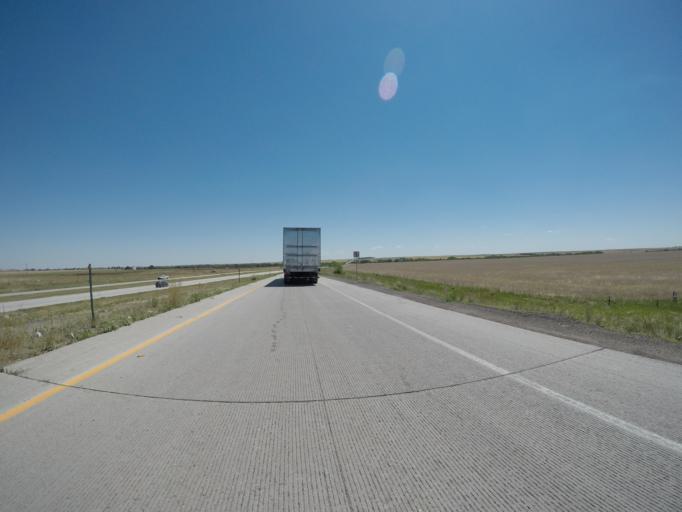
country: US
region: Colorado
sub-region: Adams County
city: Bennett
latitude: 39.7377
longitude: -104.4330
